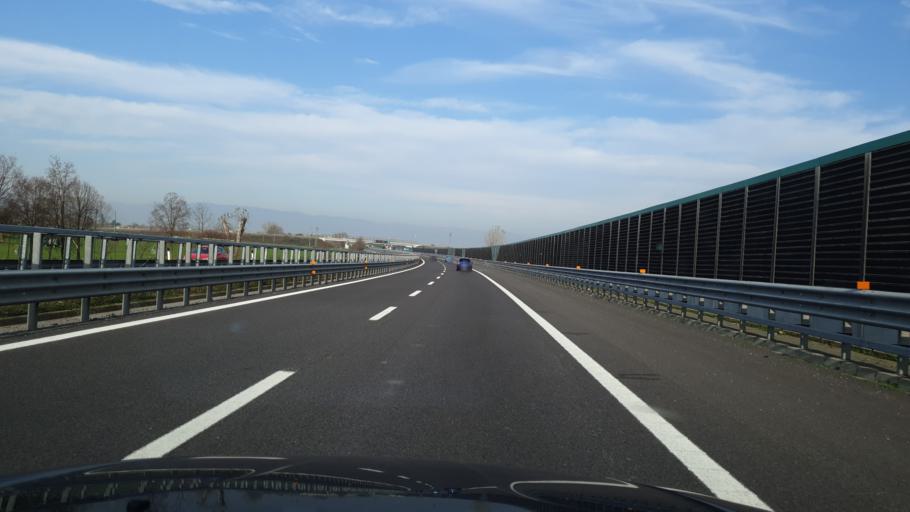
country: IT
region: Veneto
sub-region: Provincia di Vicenza
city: Torri di Quartesolo
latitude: 45.5292
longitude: 11.6276
